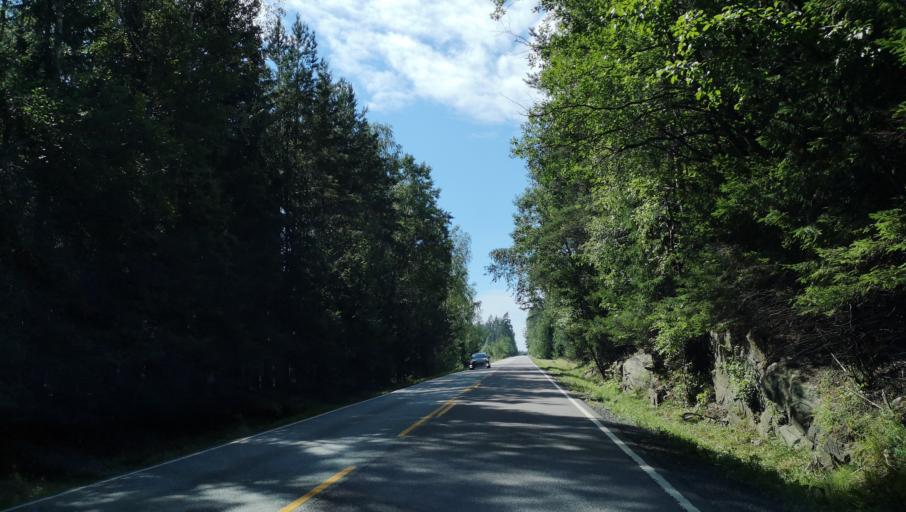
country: NO
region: Akershus
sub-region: Vestby
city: Vestby
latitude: 59.5391
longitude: 10.7708
